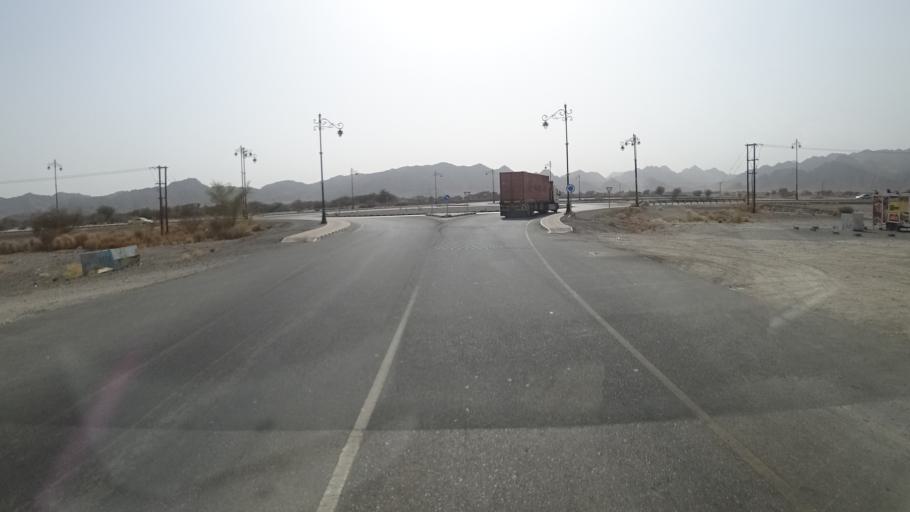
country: OM
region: Muhafazat ad Dakhiliyah
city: Nizwa
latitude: 22.9941
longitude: 57.5419
